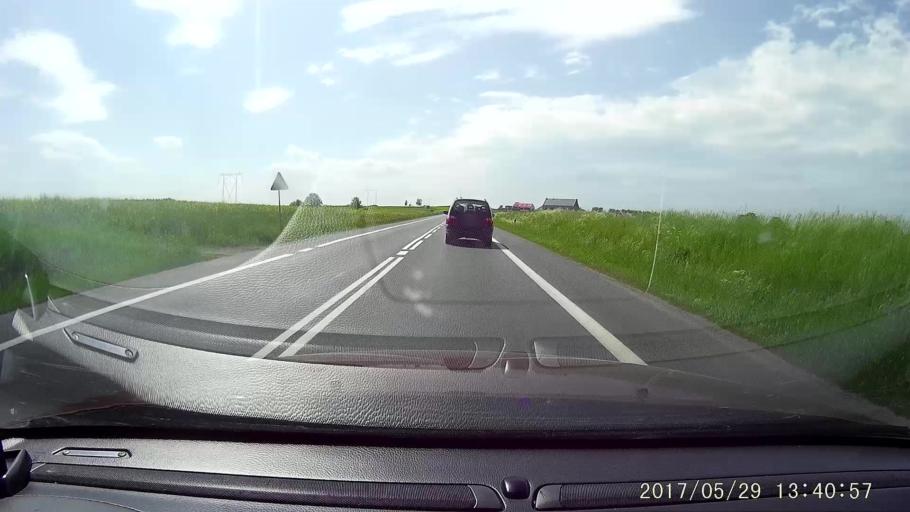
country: PL
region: Lower Silesian Voivodeship
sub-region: Powiat lubanski
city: Luban
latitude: 51.1336
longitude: 15.2658
